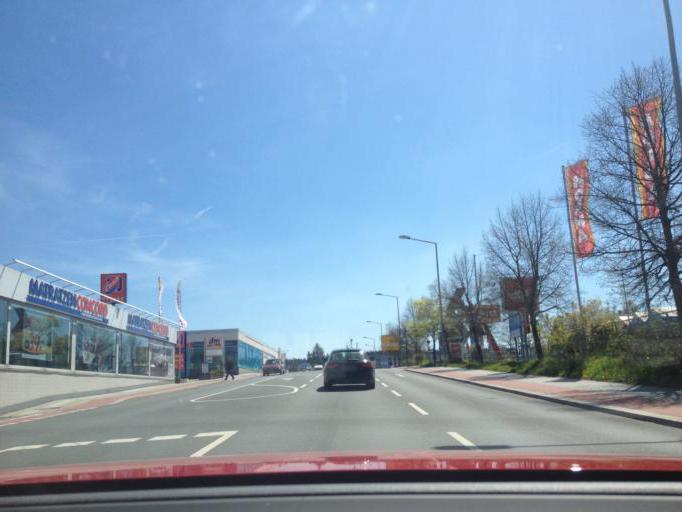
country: DE
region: Bavaria
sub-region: Upper Franconia
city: Hof
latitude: 50.3071
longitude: 11.9163
